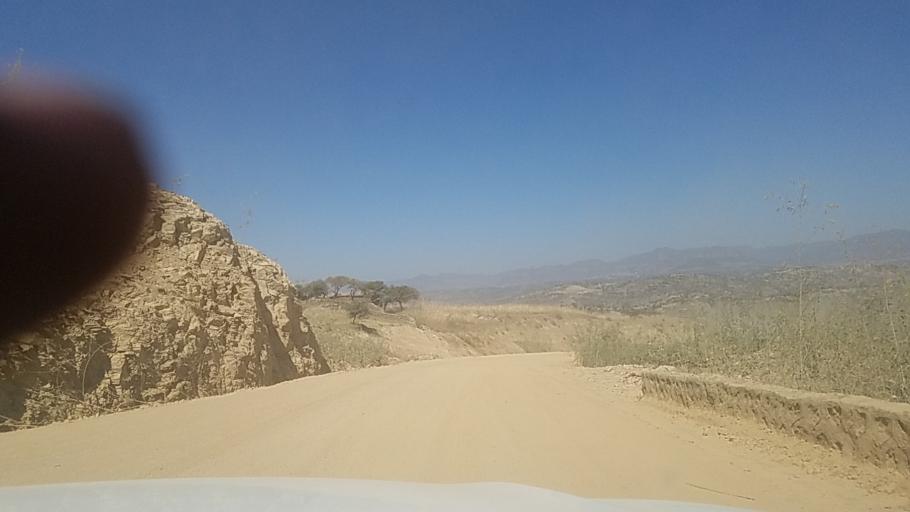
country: ET
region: Tigray
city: Adigrat
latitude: 14.0272
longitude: 39.3496
